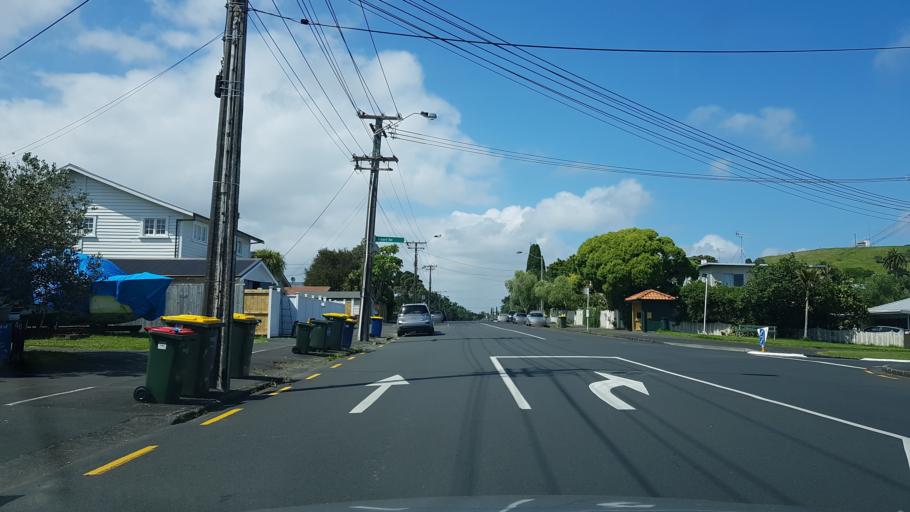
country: NZ
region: Auckland
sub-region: Auckland
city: Auckland
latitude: -36.8223
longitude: 174.8045
